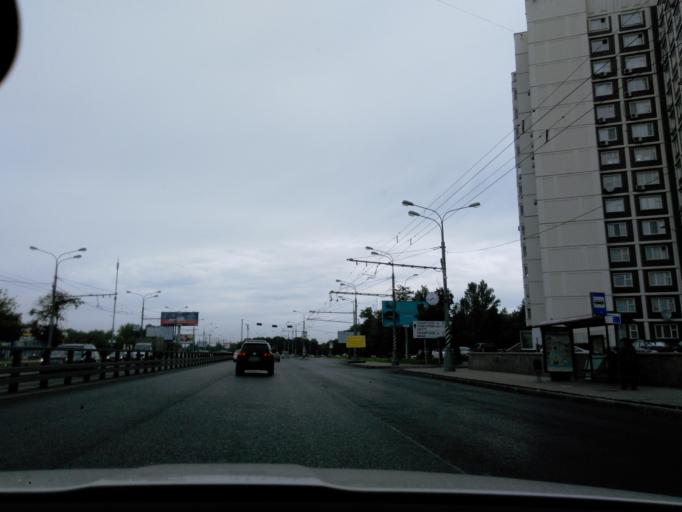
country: RU
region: Moscow
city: Tsaritsyno
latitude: 55.6477
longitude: 37.6570
